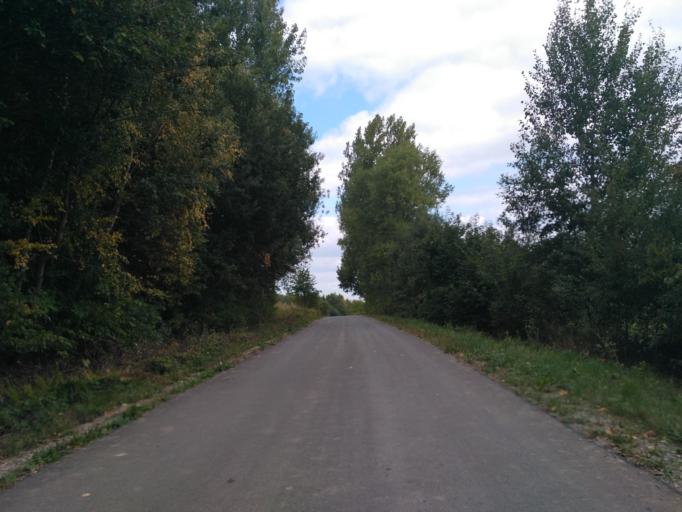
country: PL
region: Subcarpathian Voivodeship
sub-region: Powiat rzeszowski
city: Dynow
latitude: 49.7807
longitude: 22.2796
